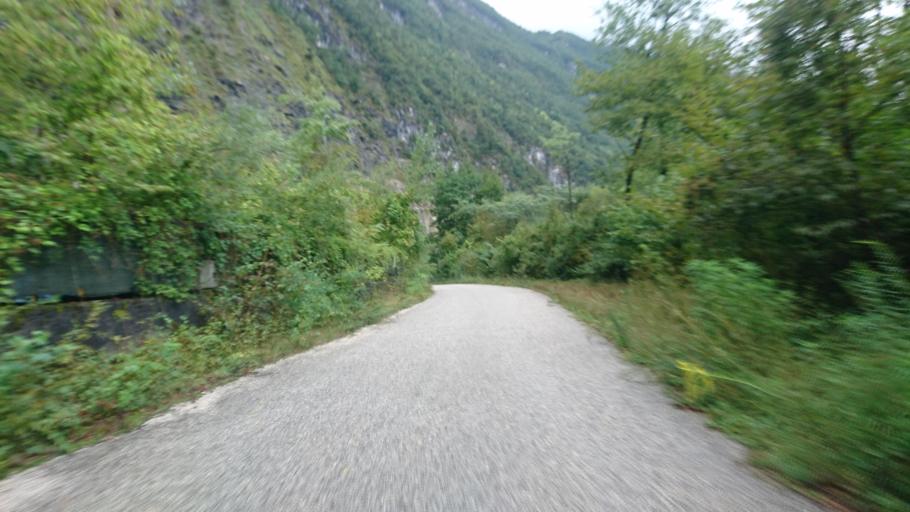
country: IT
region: Veneto
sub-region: Provincia di Vicenza
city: Enego
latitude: 45.9611
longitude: 11.6943
